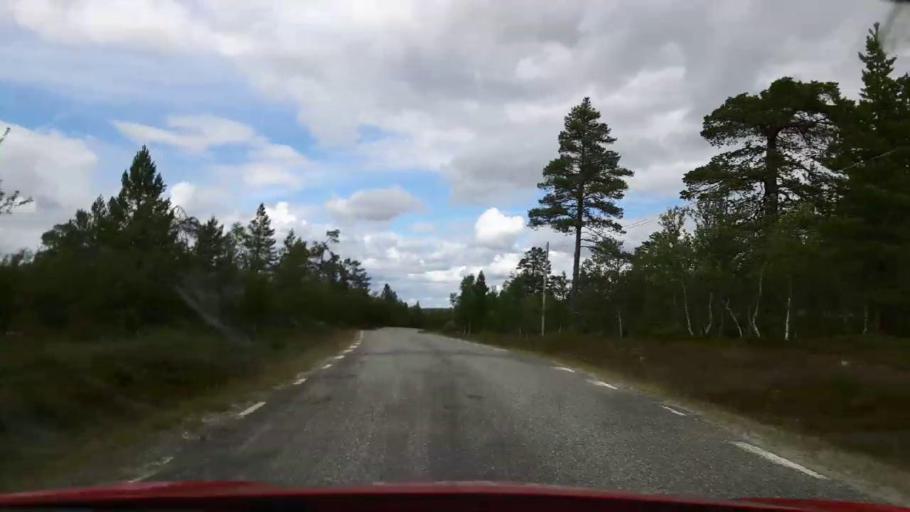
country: NO
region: Hedmark
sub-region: Engerdal
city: Engerdal
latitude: 62.3405
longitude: 12.7993
